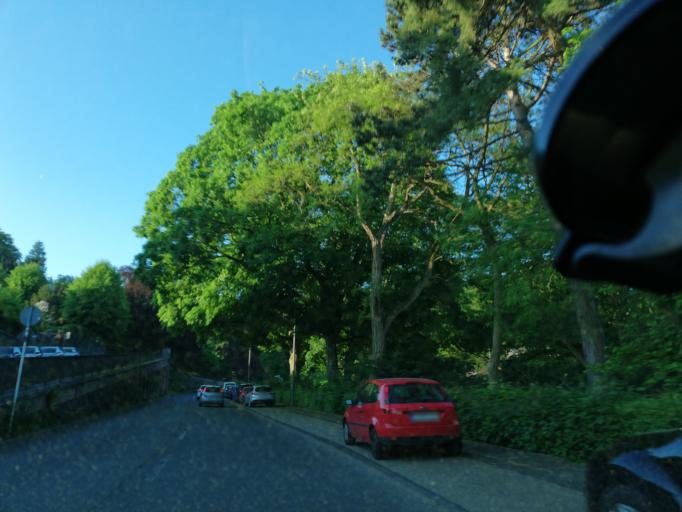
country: DE
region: North Rhine-Westphalia
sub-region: Regierungsbezirk Dusseldorf
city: Wuppertal
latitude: 51.2669
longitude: 7.2064
